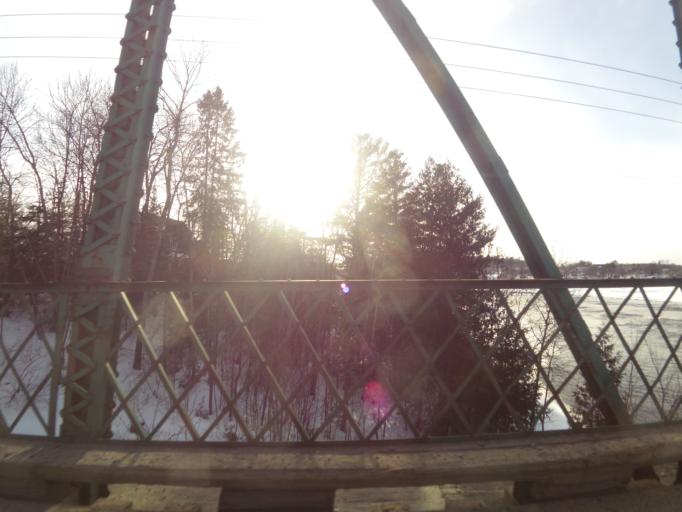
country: CA
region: Quebec
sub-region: Outaouais
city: Maniwaki
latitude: 46.2012
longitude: -75.9492
